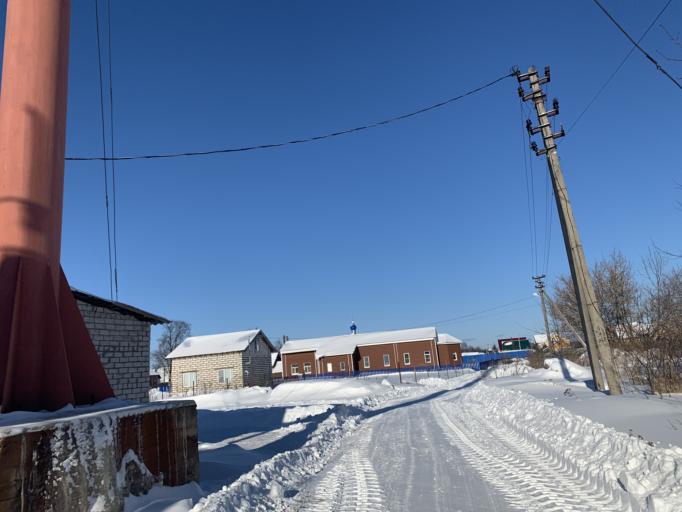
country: RU
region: Jaroslavl
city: Tunoshna
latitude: 57.6607
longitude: 40.0727
